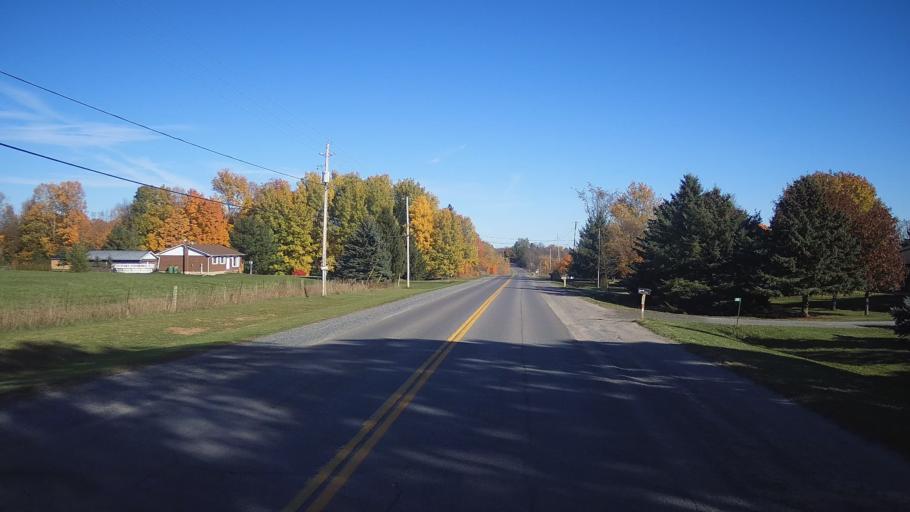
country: CA
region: Ontario
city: Kingston
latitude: 44.4071
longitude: -76.5446
